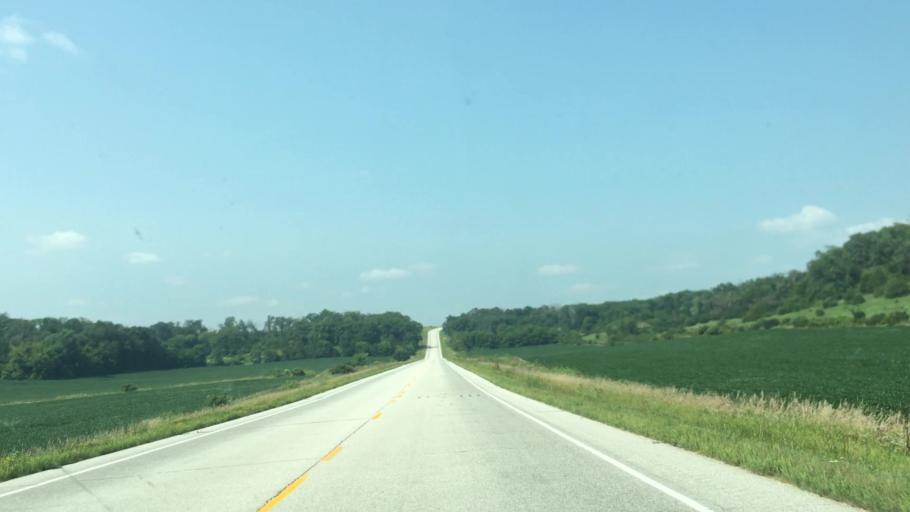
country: US
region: Minnesota
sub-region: Fillmore County
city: Harmony
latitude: 43.6322
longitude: -91.9299
